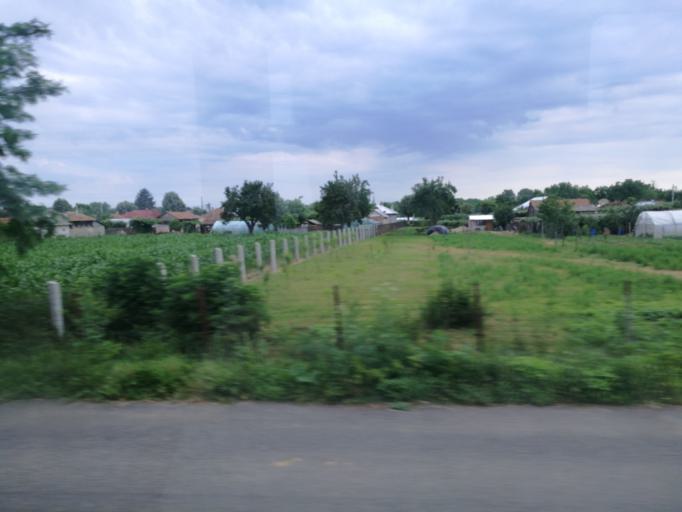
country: RO
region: Dambovita
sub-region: Oras Gaesti
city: Gaesti
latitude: 44.7156
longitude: 25.2925
